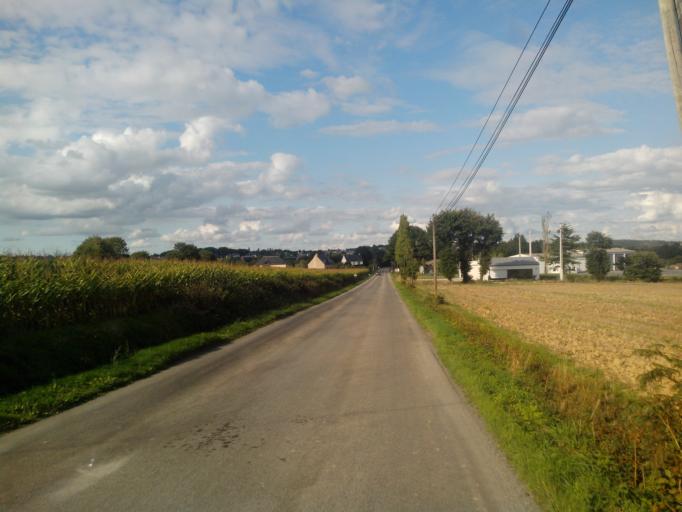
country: FR
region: Brittany
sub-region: Departement d'Ille-et-Vilaine
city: Iffendic
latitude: 48.1203
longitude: -2.0427
